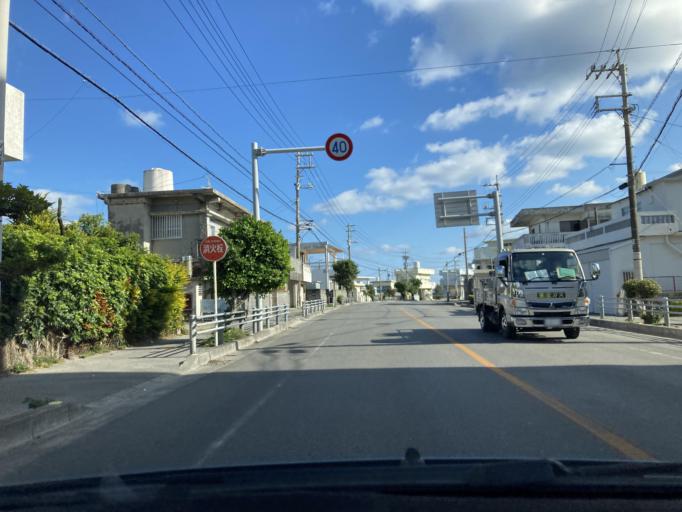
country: JP
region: Okinawa
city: Katsuren-haebaru
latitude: 26.3088
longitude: 127.9122
